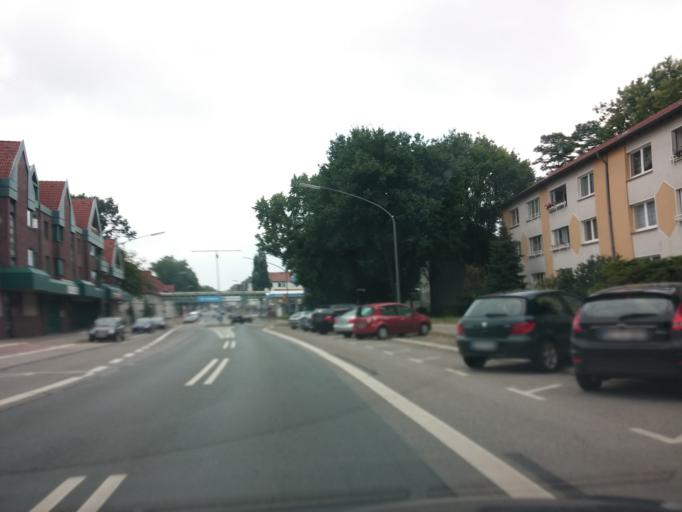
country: DE
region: North Rhine-Westphalia
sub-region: Regierungsbezirk Munster
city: Gladbeck
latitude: 51.5968
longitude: 7.0516
